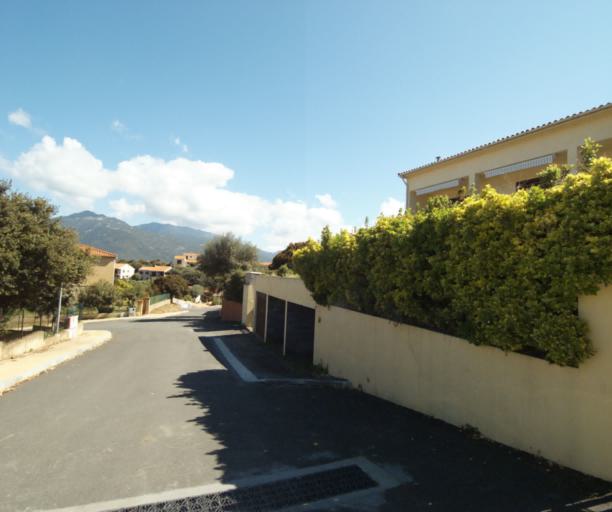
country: FR
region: Corsica
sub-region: Departement de la Corse-du-Sud
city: Propriano
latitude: 41.6742
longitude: 8.9099
